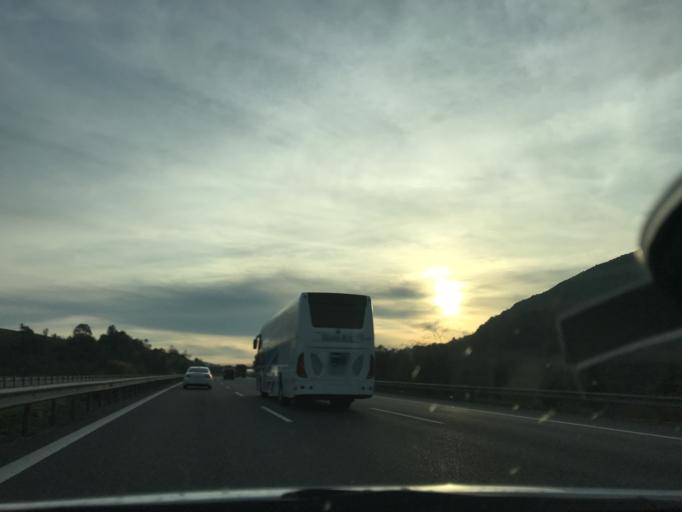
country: TR
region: Duzce
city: Gumusova
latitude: 40.8211
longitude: 30.9166
